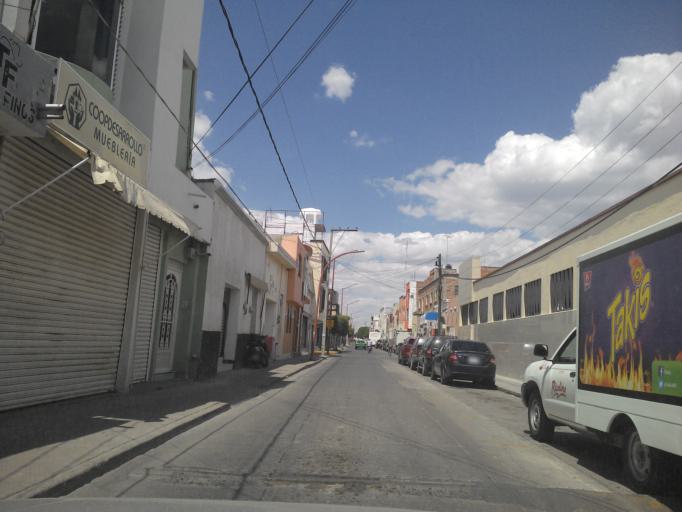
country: MX
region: Guanajuato
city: San Francisco del Rincon
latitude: 21.0198
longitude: -101.8604
